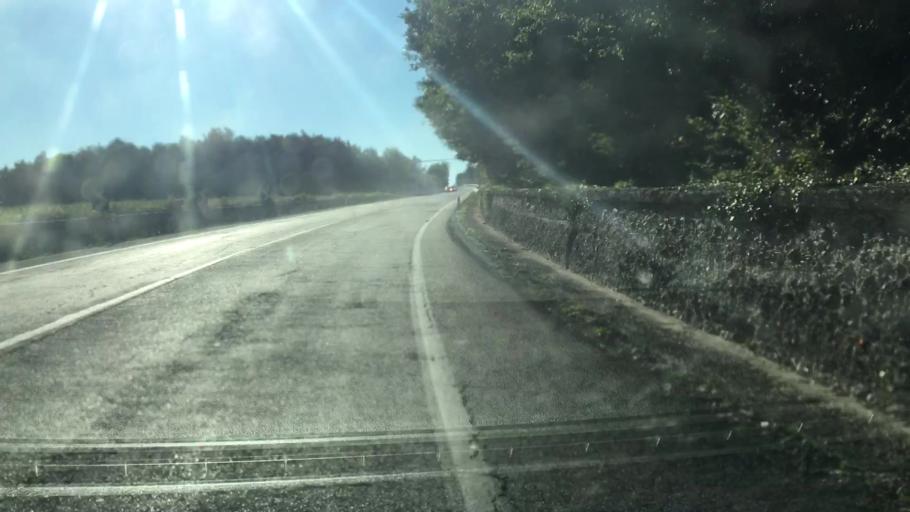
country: IT
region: Molise
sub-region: Provincia di Campobasso
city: Vinchiaturo
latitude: 41.4555
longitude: 14.5806
